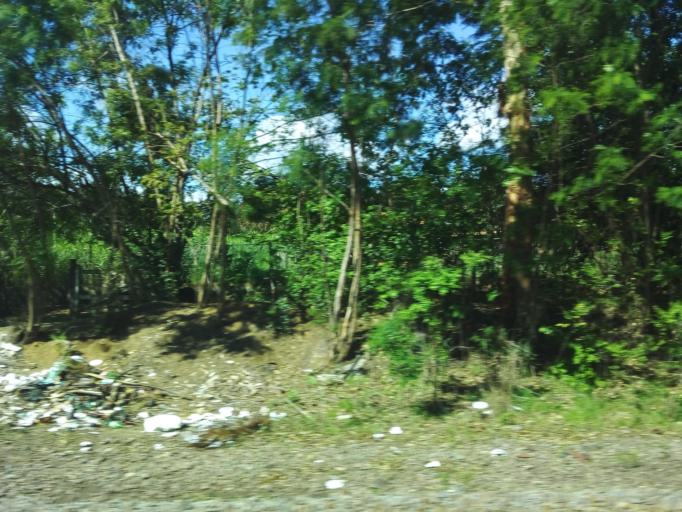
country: BR
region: Minas Gerais
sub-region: Governador Valadares
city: Governador Valadares
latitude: -18.8410
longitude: -41.8751
